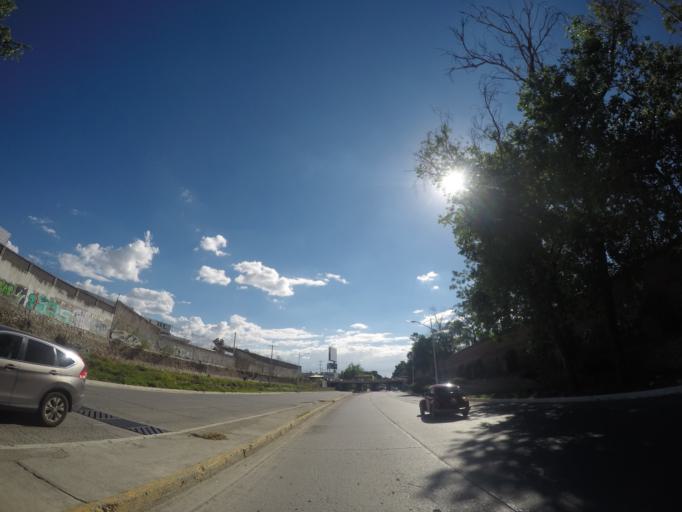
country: MX
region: San Luis Potosi
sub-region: San Luis Potosi
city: San Luis Potosi
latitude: 22.1687
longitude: -100.9795
